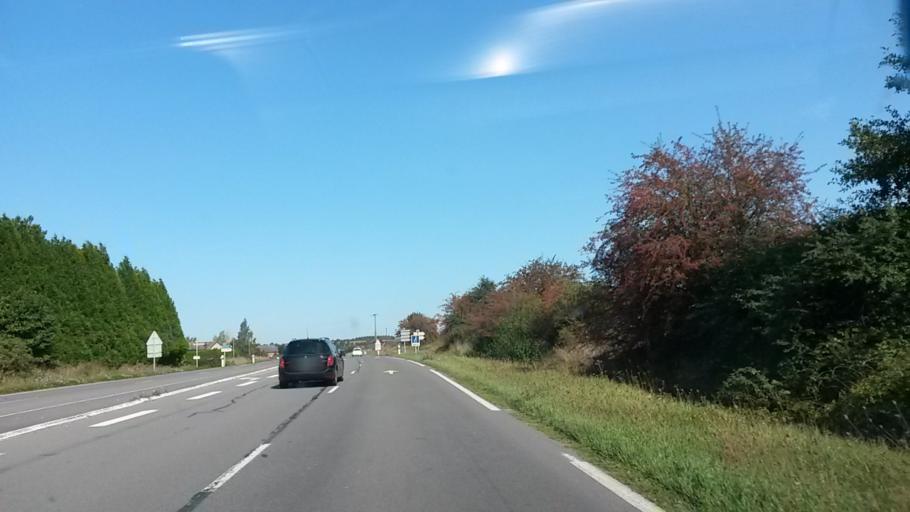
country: FR
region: Nord-Pas-de-Calais
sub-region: Departement du Nord
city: Avesnes-sur-Helpe
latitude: 50.0631
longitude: 3.9321
